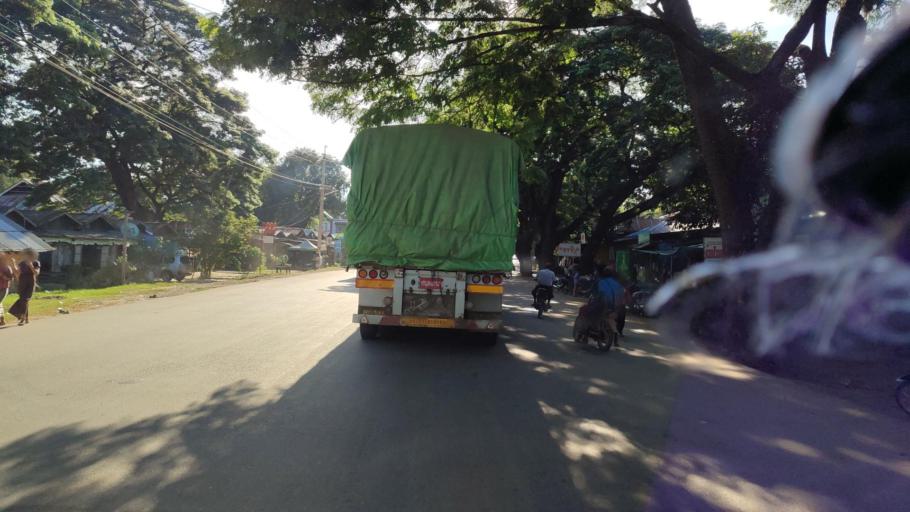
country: MM
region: Mandalay
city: Yamethin
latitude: 20.7583
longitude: 96.3158
